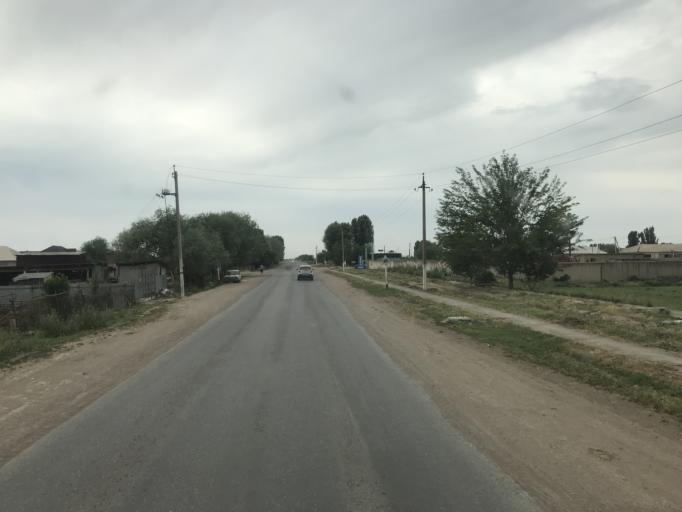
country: KZ
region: Ongtustik Qazaqstan
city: Asykata
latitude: 40.9051
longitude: 68.3548
